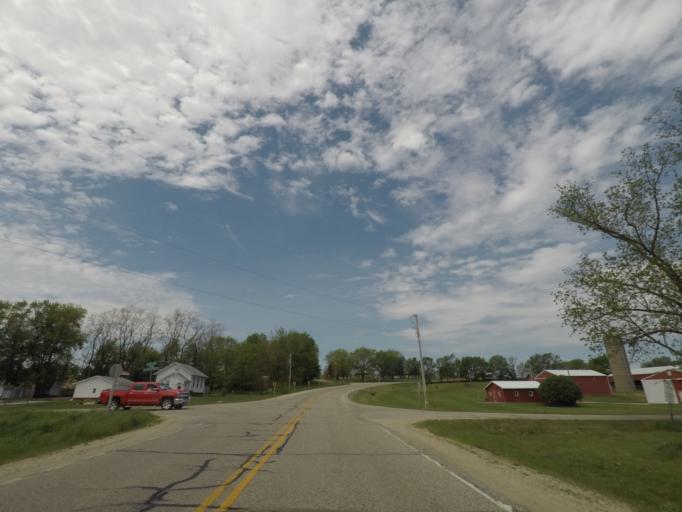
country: US
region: Wisconsin
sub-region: Rock County
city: Orfordville
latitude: 42.5996
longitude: -89.2081
